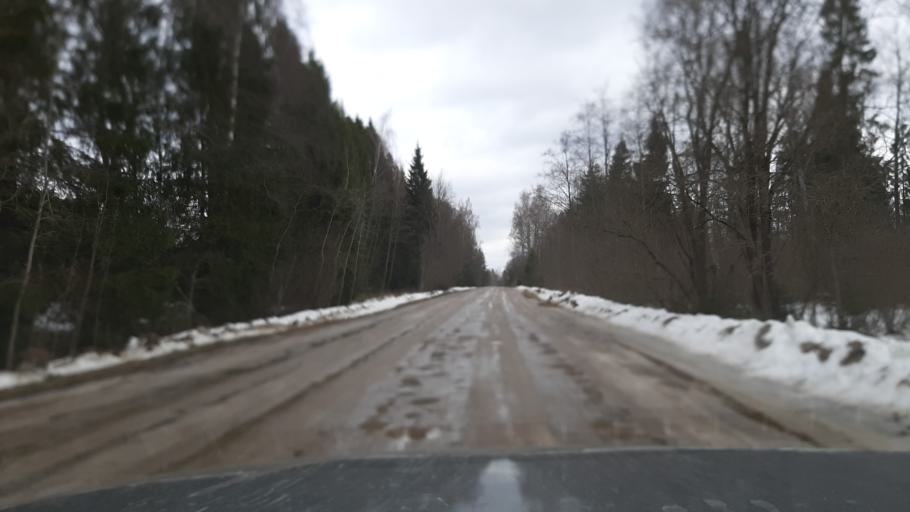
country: RU
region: Ivanovo
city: Teykovo
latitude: 56.8883
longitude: 40.6564
